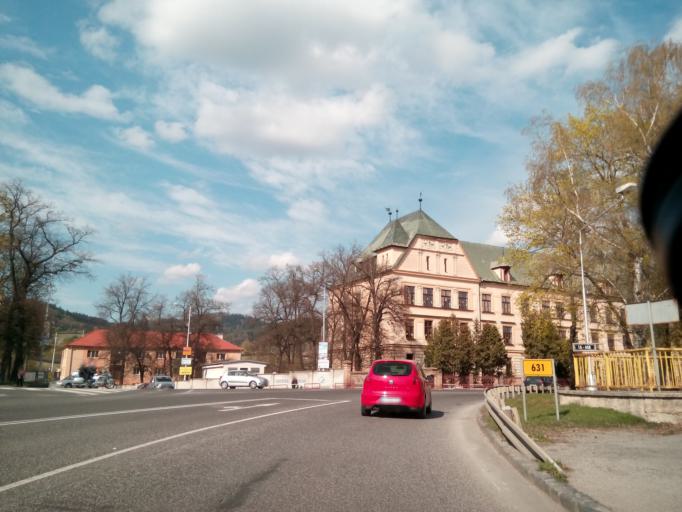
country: SK
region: Presovsky
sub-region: Okres Presov
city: Levoca
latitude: 49.0268
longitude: 20.5939
